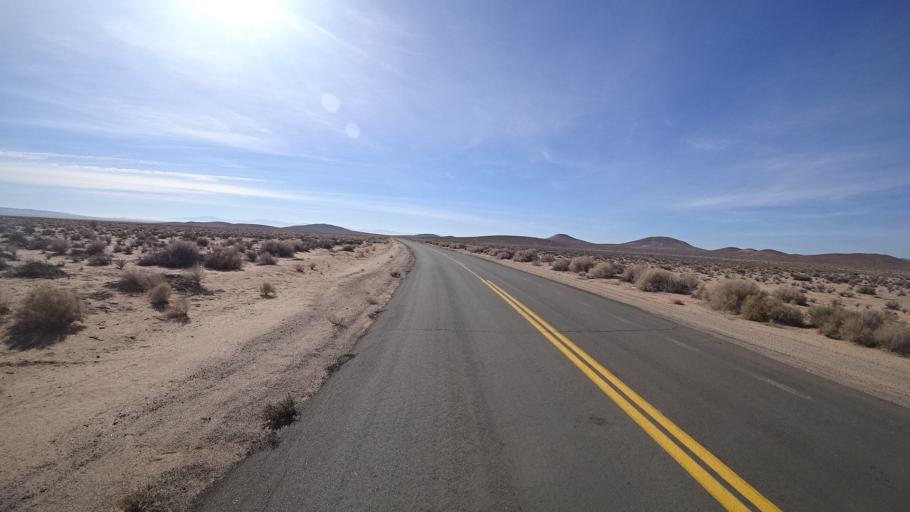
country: US
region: California
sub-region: Kern County
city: North Edwards
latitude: 35.0711
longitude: -117.8030
